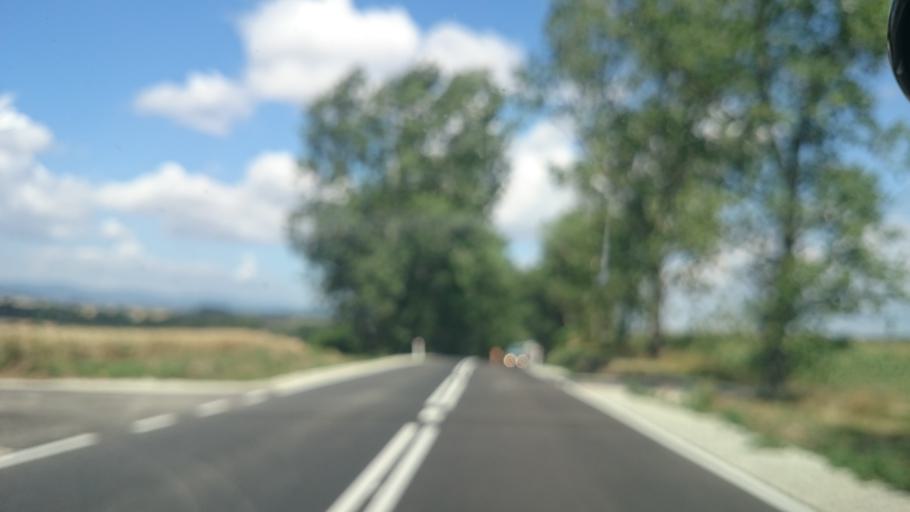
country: PL
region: Lower Silesian Voivodeship
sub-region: Powiat zabkowicki
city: Kamieniec Zabkowicki
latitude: 50.5582
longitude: 16.8523
